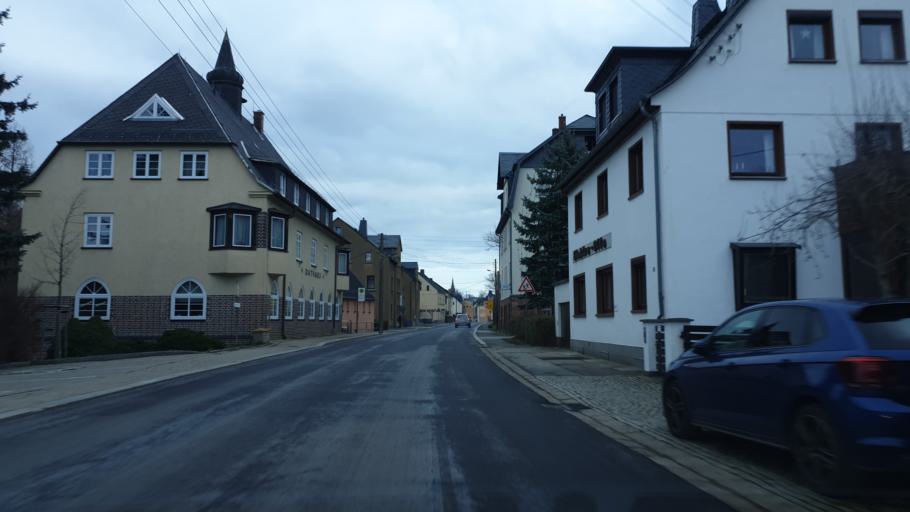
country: DE
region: Saxony
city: Bernsdorf
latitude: 50.7442
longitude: 12.6537
